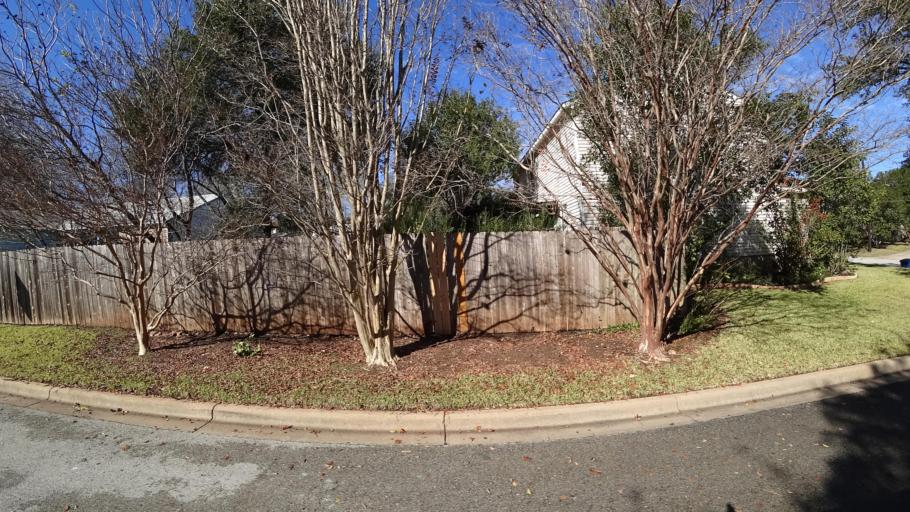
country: US
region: Texas
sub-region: Travis County
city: Wells Branch
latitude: 30.4297
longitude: -97.7127
